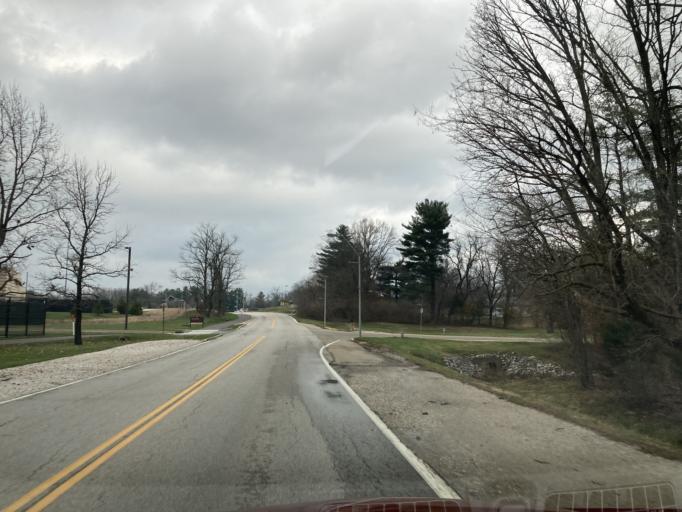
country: US
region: Indiana
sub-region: Monroe County
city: Bloomington
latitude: 39.1833
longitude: -86.5192
